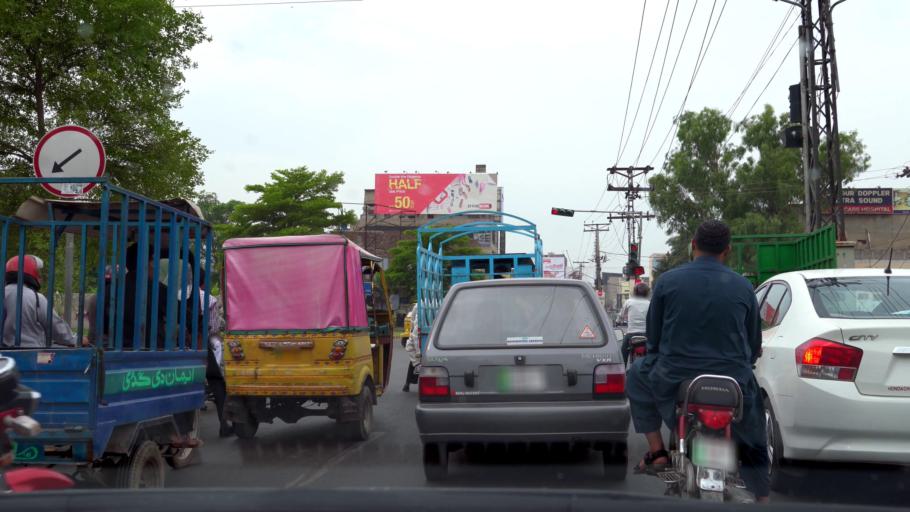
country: PK
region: Punjab
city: Faisalabad
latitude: 31.4246
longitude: 73.0711
